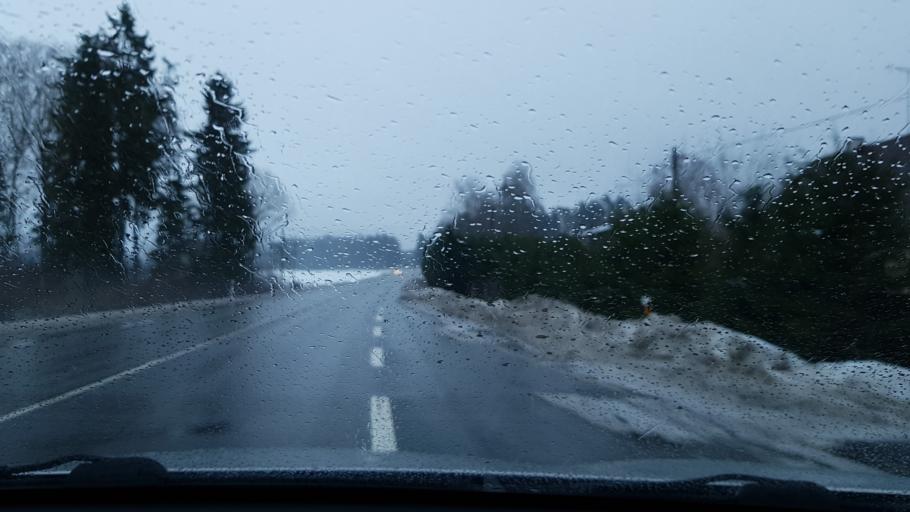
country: EE
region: Raplamaa
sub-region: Maerjamaa vald
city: Marjamaa
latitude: 58.9292
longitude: 24.4788
